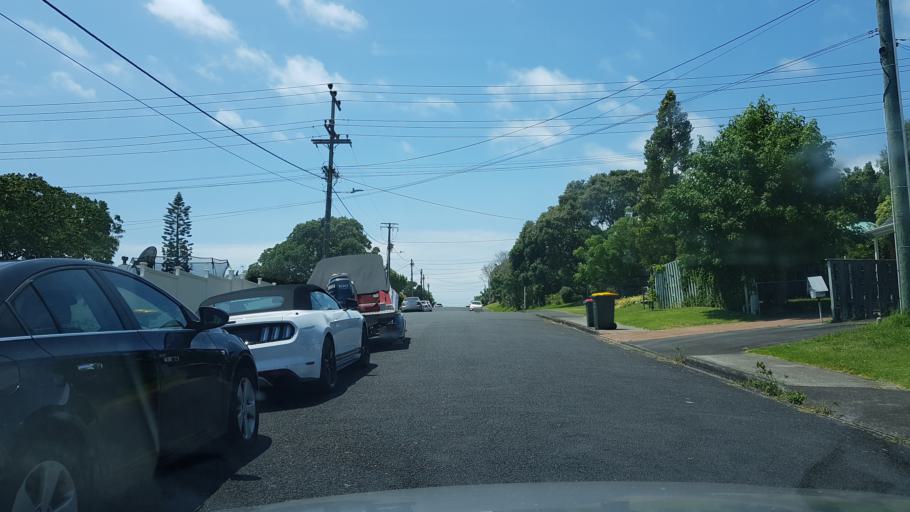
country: NZ
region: Auckland
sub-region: Auckland
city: North Shore
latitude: -36.8150
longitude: 174.7878
